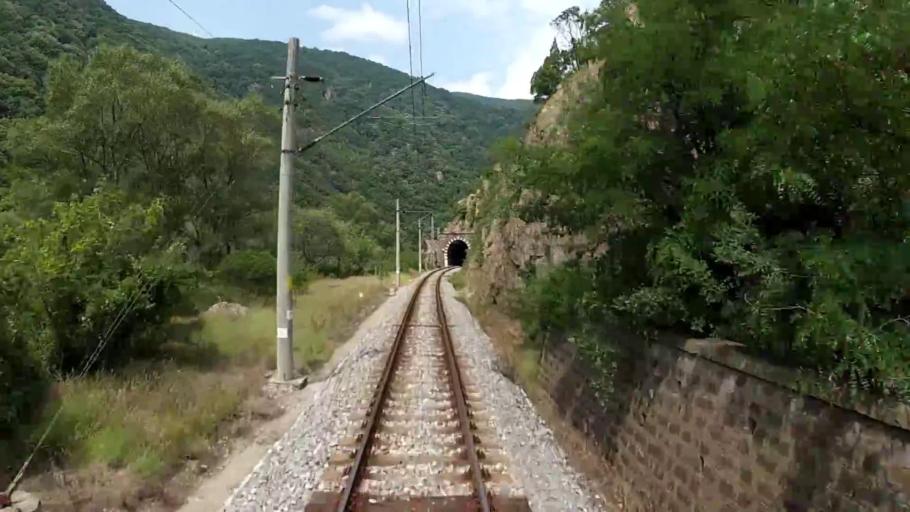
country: BG
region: Blagoevgrad
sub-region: Obshtina Kresna
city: Stara Kresna
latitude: 41.8144
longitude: 23.1597
